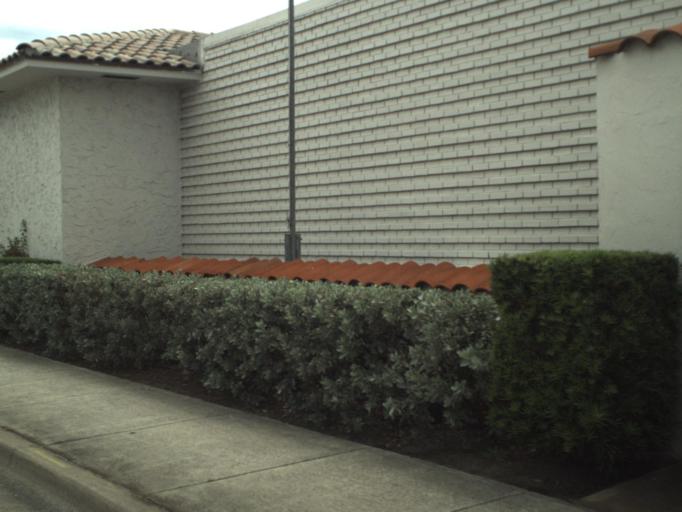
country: US
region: Florida
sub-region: Palm Beach County
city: Riviera Beach
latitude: 26.7606
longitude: -80.0553
